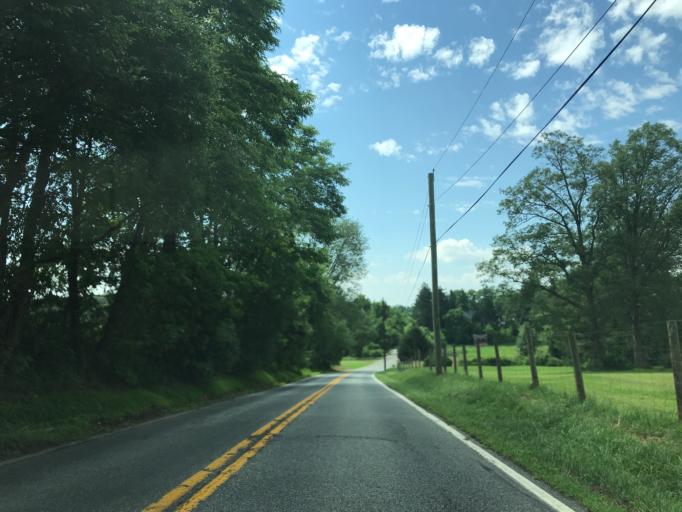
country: US
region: Pennsylvania
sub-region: York County
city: Susquehanna Trails
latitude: 39.7126
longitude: -76.4298
